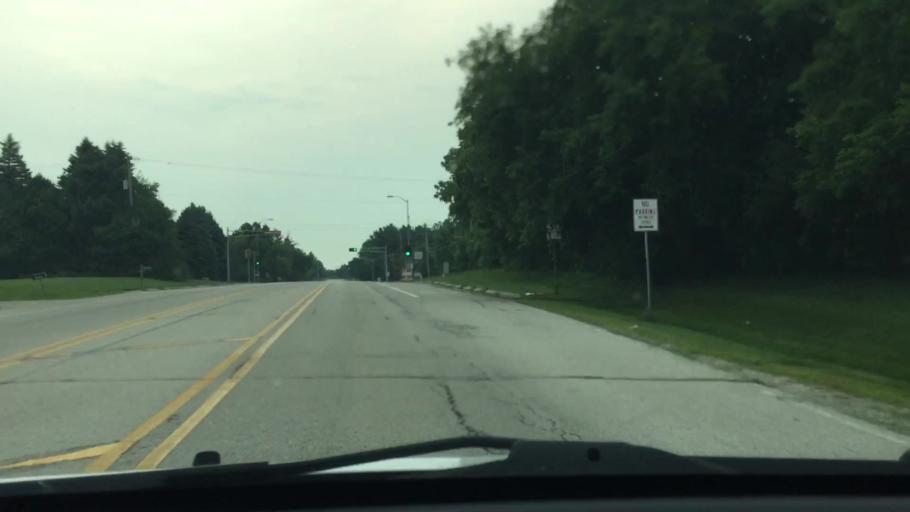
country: US
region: Wisconsin
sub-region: Waukesha County
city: New Berlin
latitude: 42.9908
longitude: -88.1488
